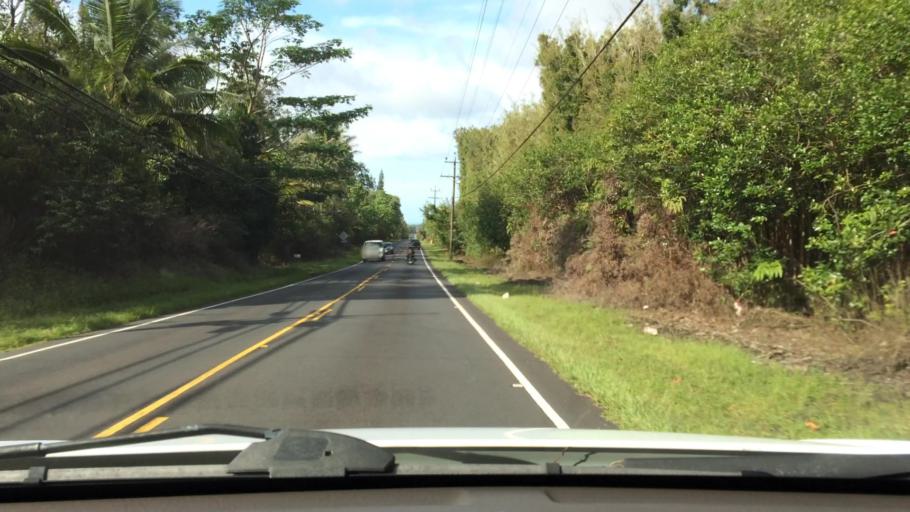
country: US
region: Hawaii
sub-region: Hawaii County
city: Hawaiian Paradise Park
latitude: 19.5092
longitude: -154.9464
